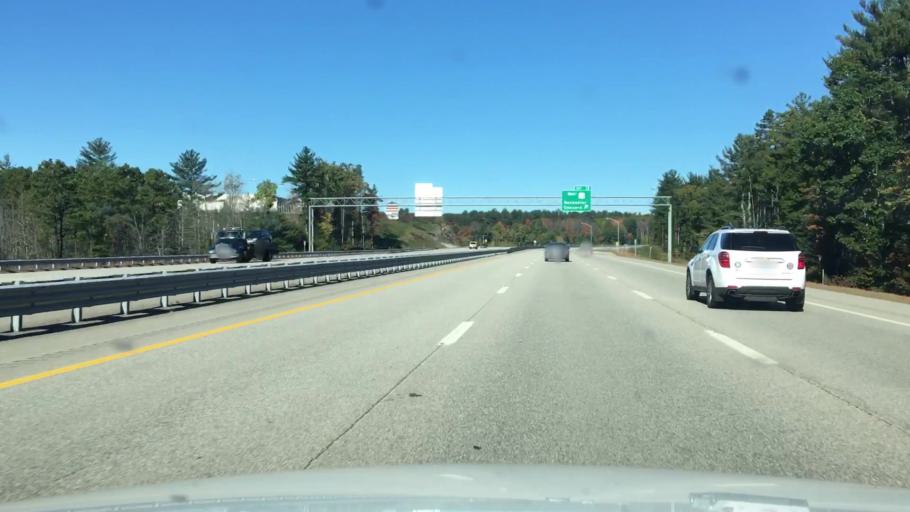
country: US
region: New Hampshire
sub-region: Strafford County
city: Rochester
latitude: 43.2909
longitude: -70.9897
